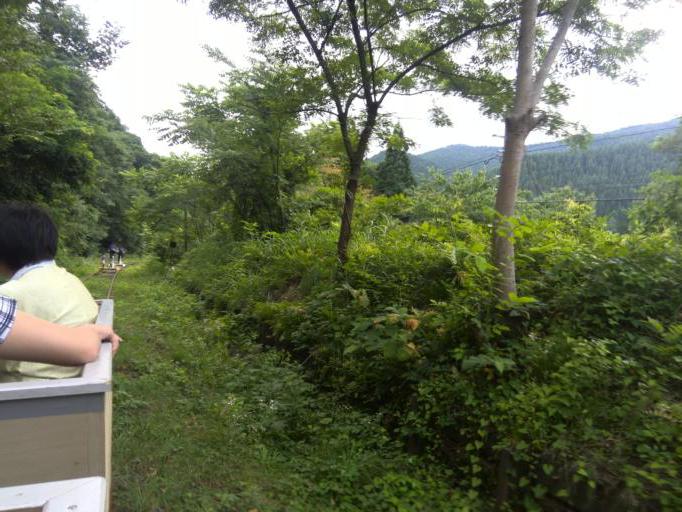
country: JP
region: Akita
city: Odate
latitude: 40.2975
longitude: 140.6420
